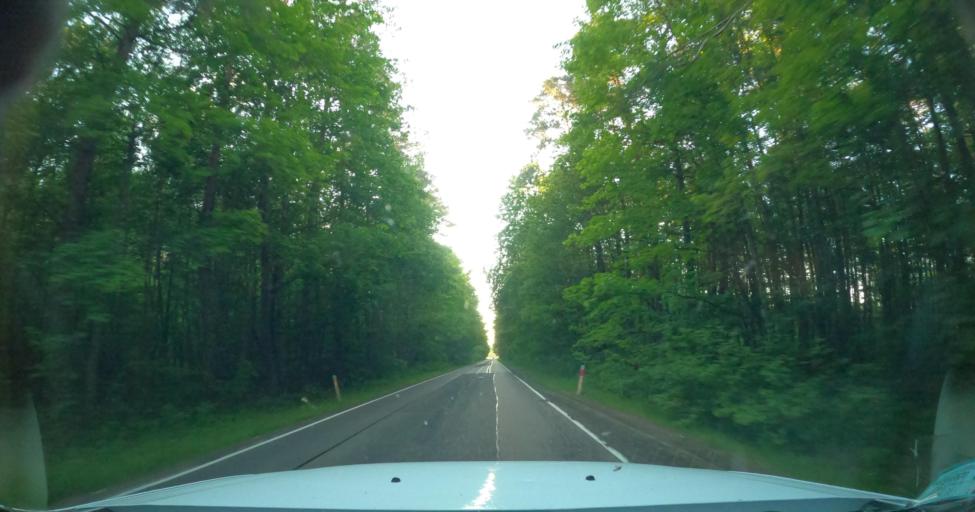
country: PL
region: Pomeranian Voivodeship
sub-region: Powiat bytowski
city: Czarna Dabrowka
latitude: 54.3813
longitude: 17.4879
